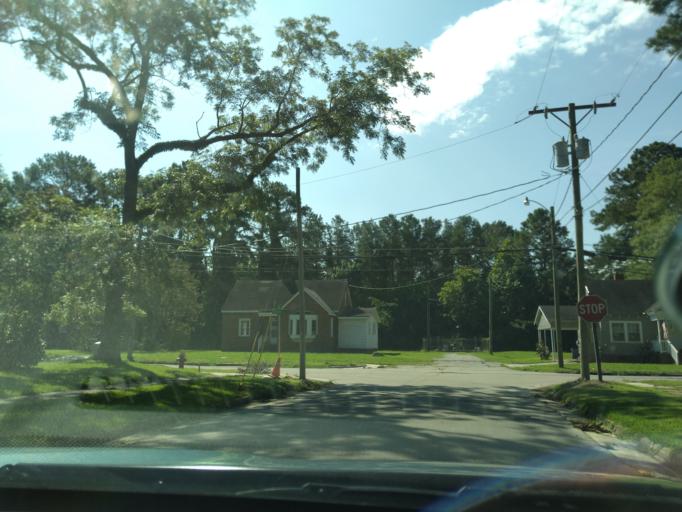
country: US
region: North Carolina
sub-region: Washington County
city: Plymouth
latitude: 35.8601
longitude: -76.7484
